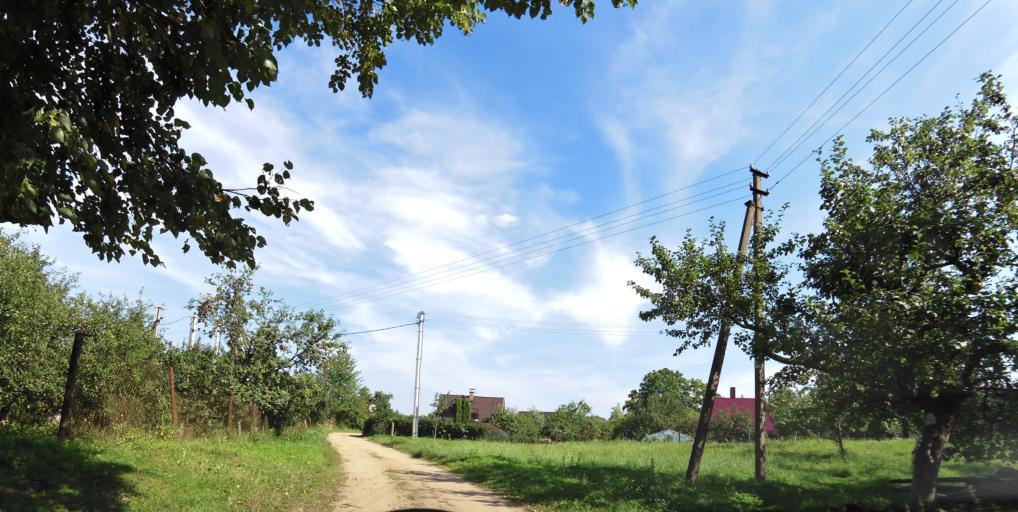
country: LT
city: Grigiskes
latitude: 54.7491
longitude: 25.0235
